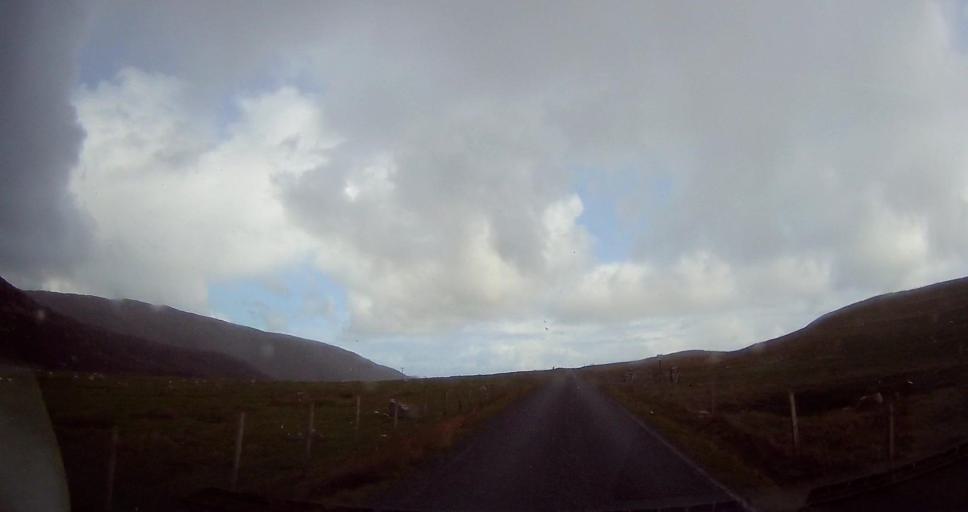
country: GB
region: Scotland
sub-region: Shetland Islands
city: Lerwick
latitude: 60.5541
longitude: -1.3402
